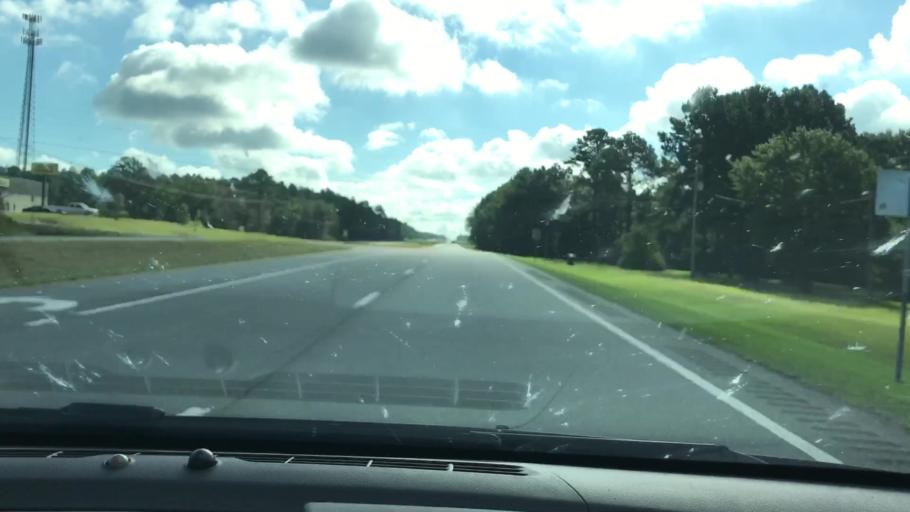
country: US
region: Georgia
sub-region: Worth County
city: Sylvester
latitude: 31.5517
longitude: -83.9382
